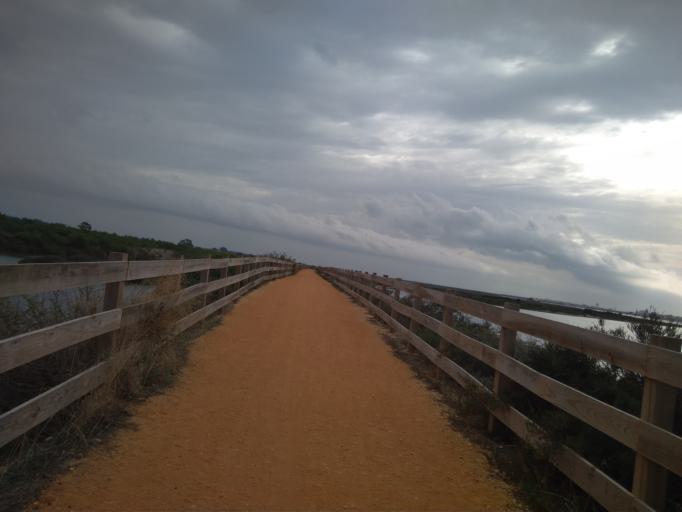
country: PT
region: Faro
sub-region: Faro
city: Faro
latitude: 37.0195
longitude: -8.0024
